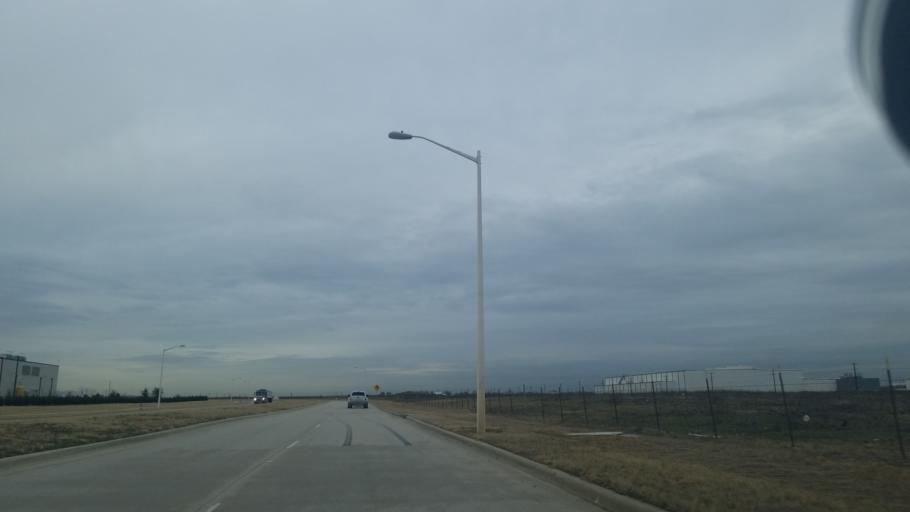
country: US
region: Texas
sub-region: Denton County
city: Denton
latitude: 33.2110
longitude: -97.1844
